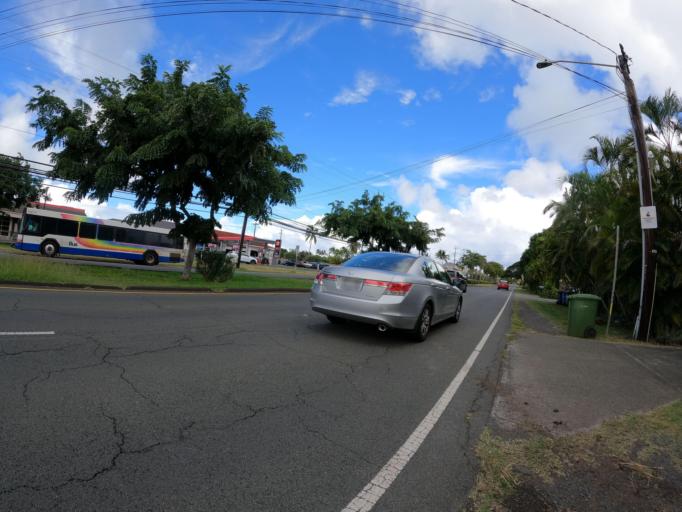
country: US
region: Hawaii
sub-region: Honolulu County
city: Kailua
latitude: 21.4222
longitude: -157.7473
